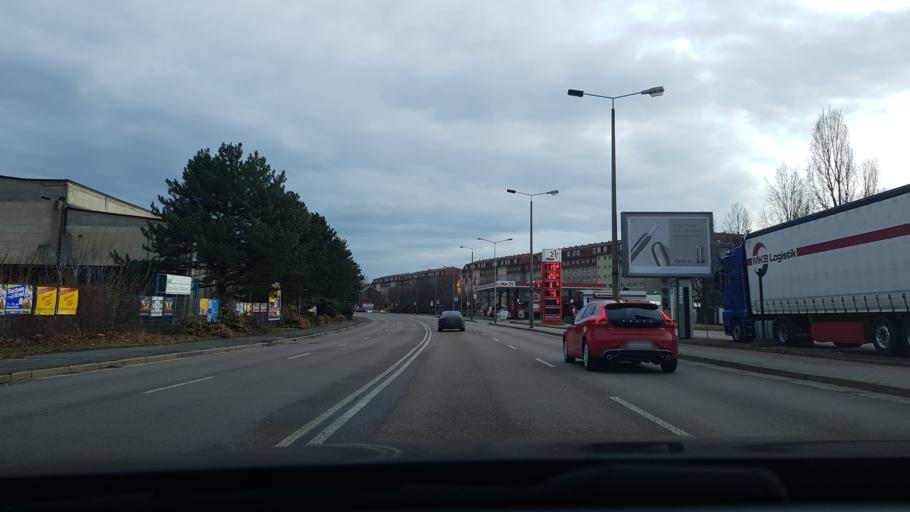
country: DE
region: Saxony
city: Heidenau
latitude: 50.9733
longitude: 13.8627
